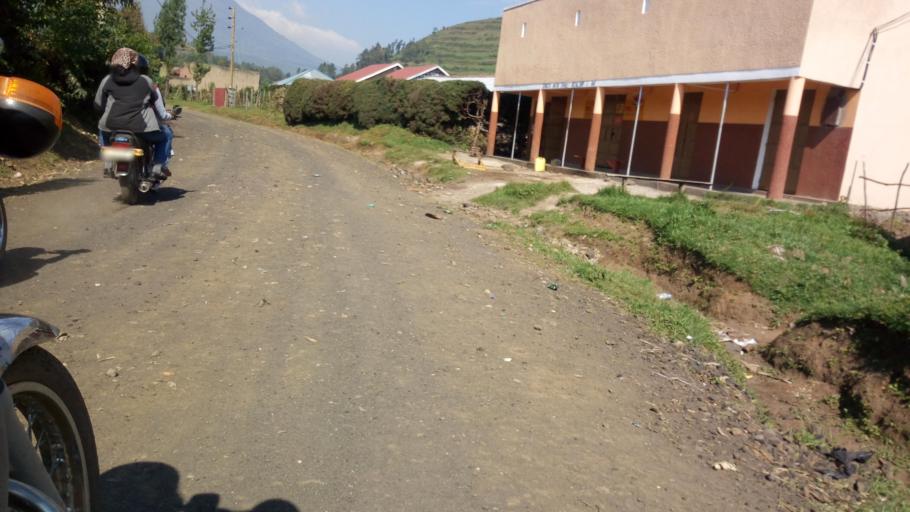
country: UG
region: Western Region
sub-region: Kisoro District
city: Kisoro
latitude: -1.3329
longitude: 29.6376
